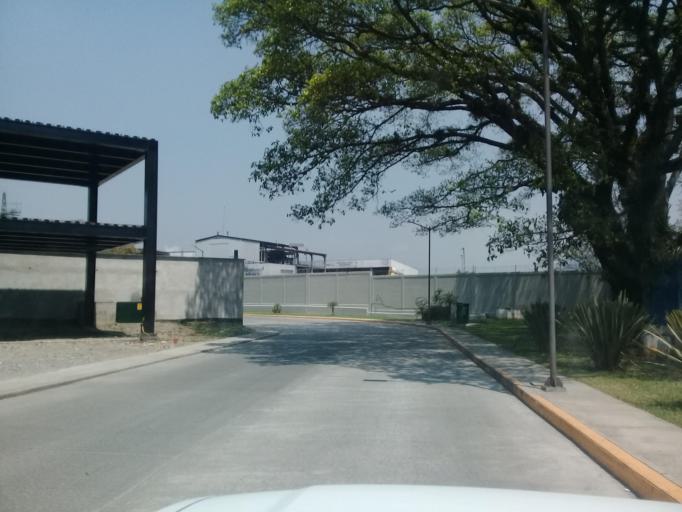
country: MX
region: Veracruz
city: Ixtac Zoquitlan
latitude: 18.8615
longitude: -97.0612
